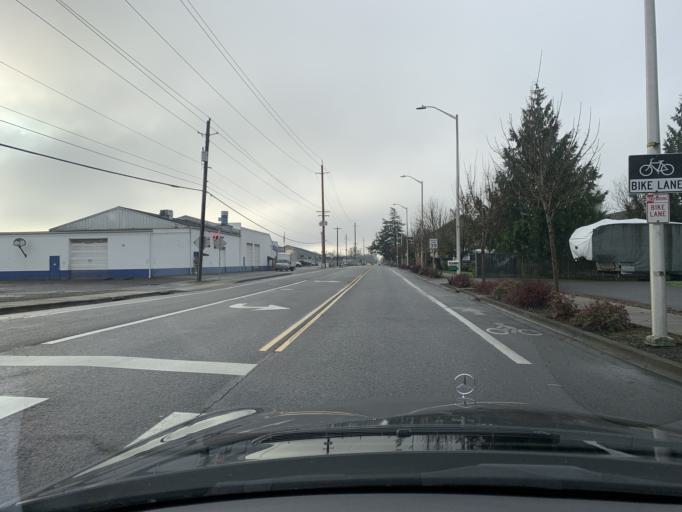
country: US
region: Washington
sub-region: Clark County
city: Battle Ground
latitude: 45.7754
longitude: -122.5270
